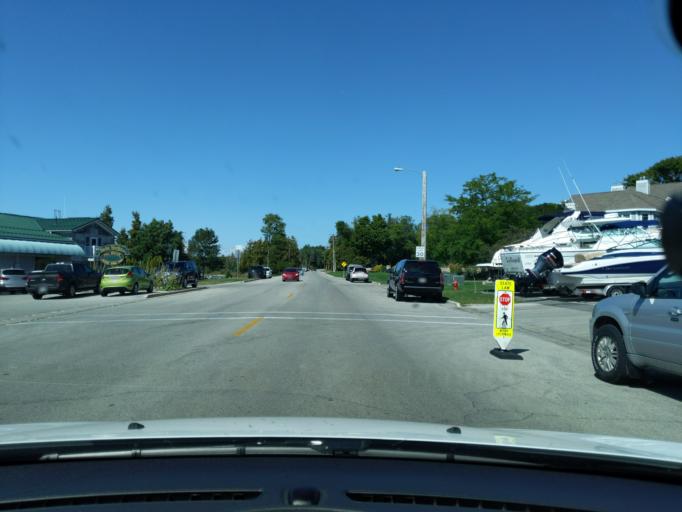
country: US
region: Wisconsin
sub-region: Door County
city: Sturgeon Bay
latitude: 45.2026
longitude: -87.1188
